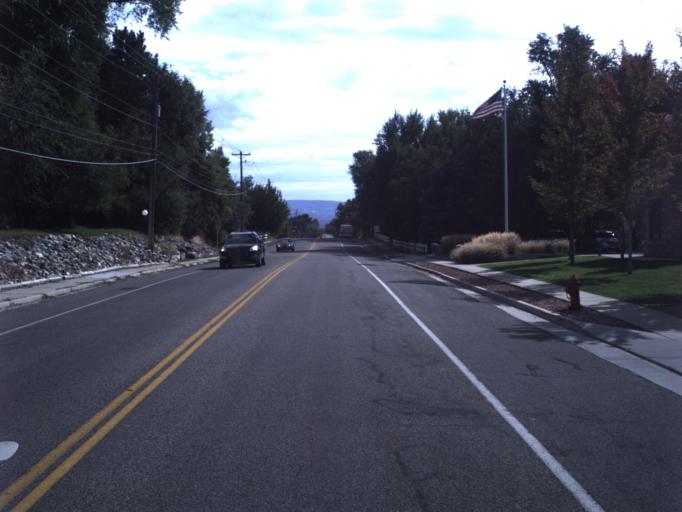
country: US
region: Utah
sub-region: Davis County
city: Farmington
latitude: 40.9760
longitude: -111.8833
